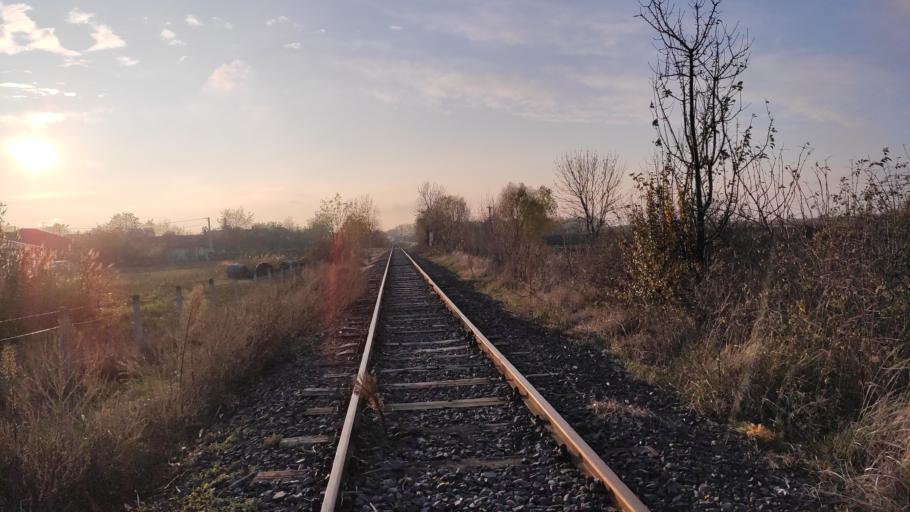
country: HU
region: Bekes
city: Mezobereny
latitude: 46.7648
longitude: 21.0463
